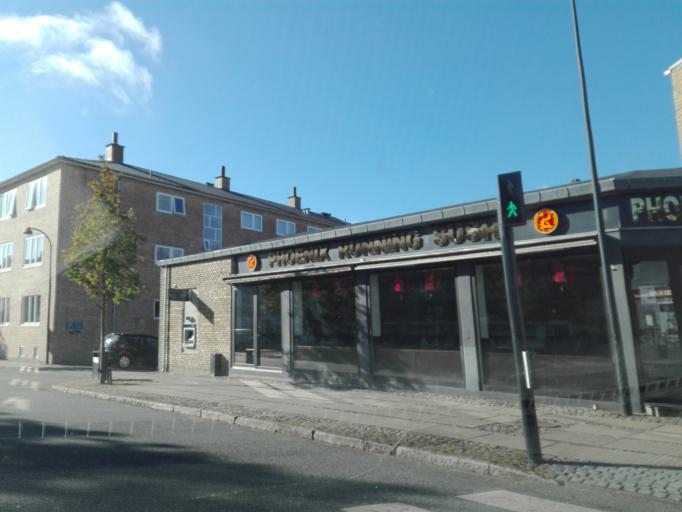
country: DK
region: Capital Region
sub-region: Lyngby-Tarbaek Kommune
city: Kongens Lyngby
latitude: 55.7495
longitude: 12.5182
